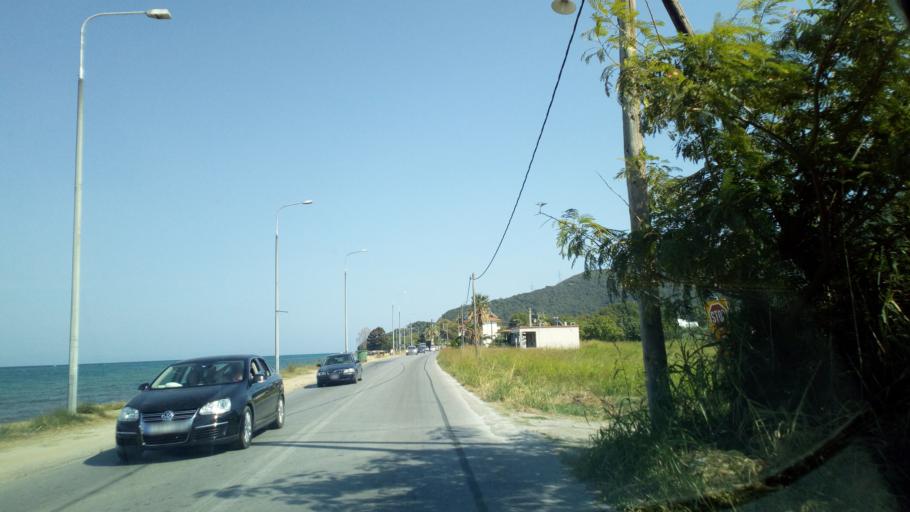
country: GR
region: Central Macedonia
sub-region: Nomos Thessalonikis
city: Stavros
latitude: 40.6614
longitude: 23.7210
